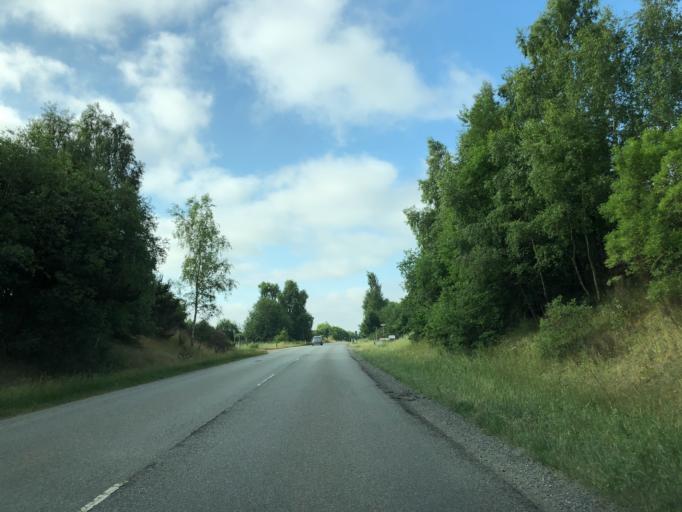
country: DK
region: South Denmark
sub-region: Kolding Kommune
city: Kolding
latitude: 55.5633
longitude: 9.4393
